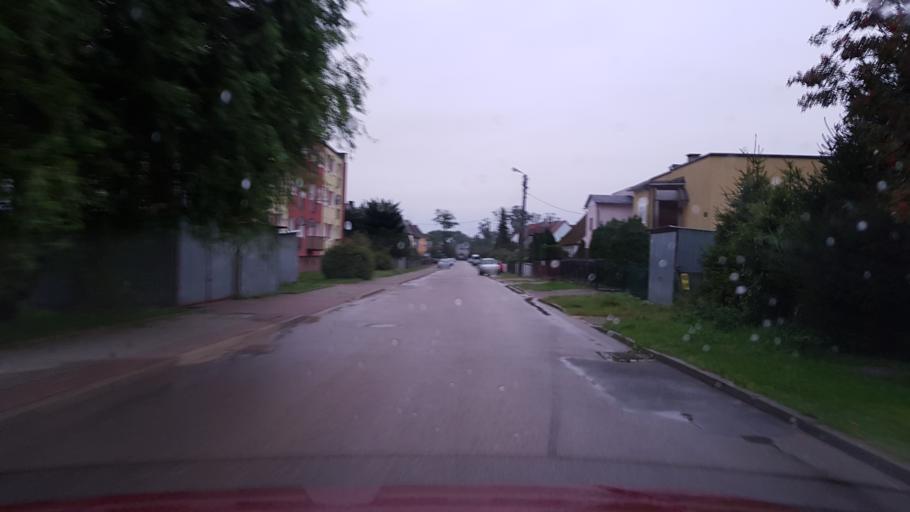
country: PL
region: West Pomeranian Voivodeship
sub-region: Powiat slawienski
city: Slawno
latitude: 54.3454
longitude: 16.6762
